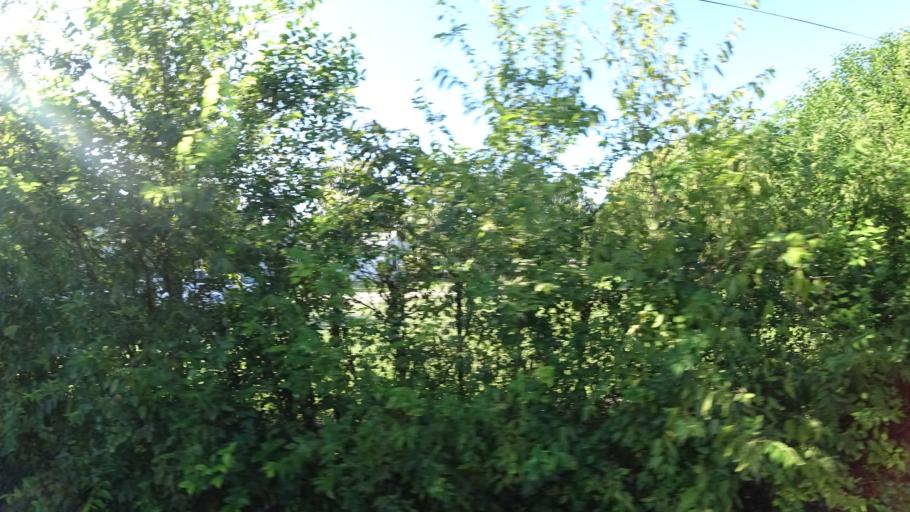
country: US
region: Texas
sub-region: Travis County
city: Wells Branch
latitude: 30.3528
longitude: -97.6985
